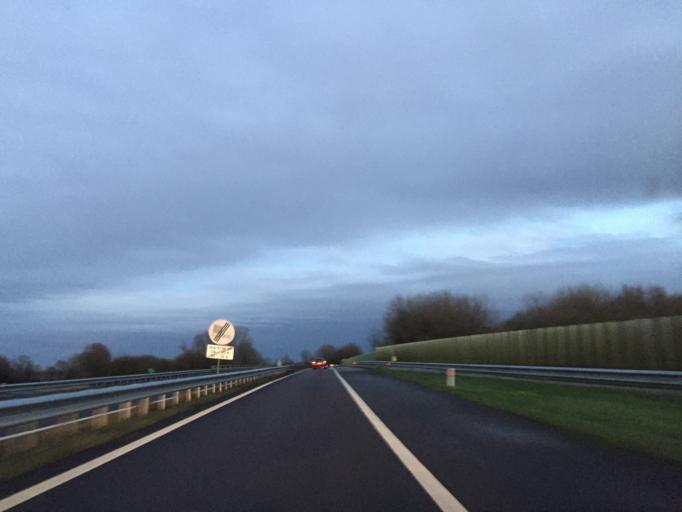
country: NL
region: North Brabant
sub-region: Gemeente Moerdijk
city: Klundert
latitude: 51.6353
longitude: 4.5406
